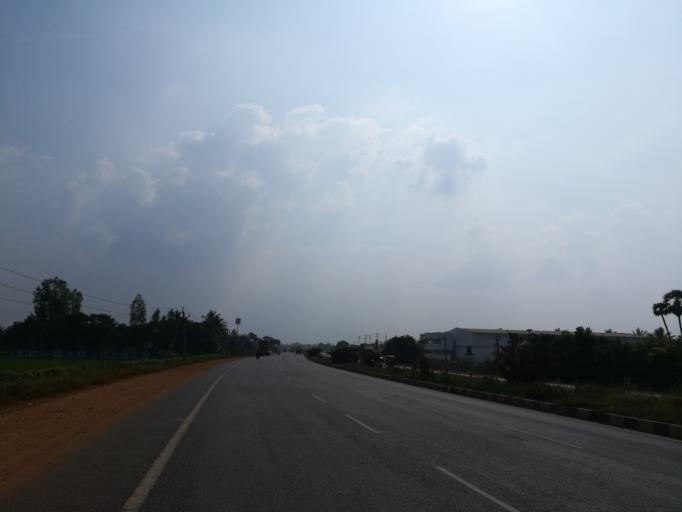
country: IN
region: Andhra Pradesh
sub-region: Nellore
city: Kovur
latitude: 14.5348
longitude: 79.9916
